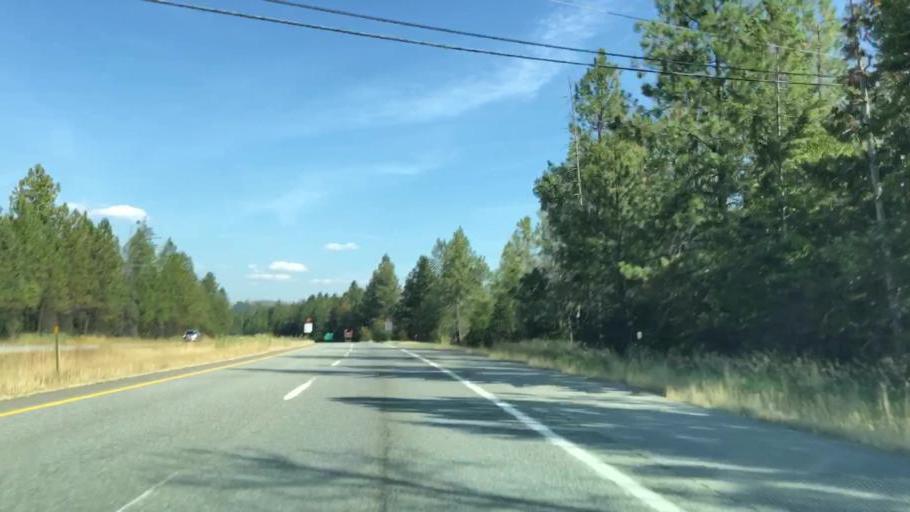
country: US
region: Idaho
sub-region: Shoshone County
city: Pinehurst
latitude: 47.5506
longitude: -116.3022
